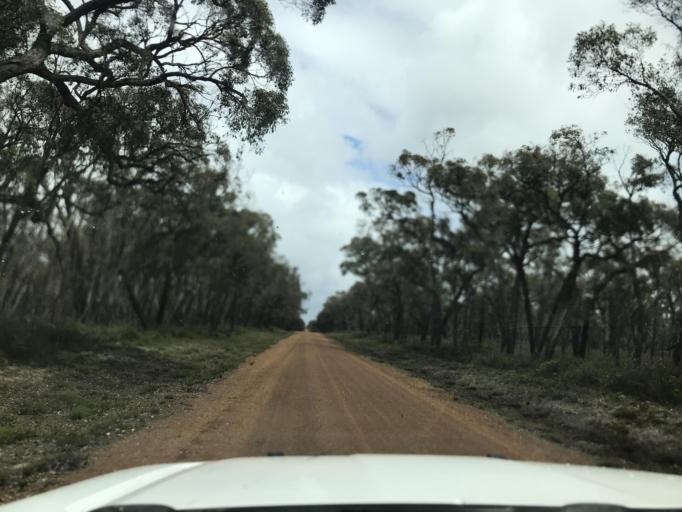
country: AU
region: South Australia
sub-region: Wattle Range
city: Penola
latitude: -37.2953
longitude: 141.3195
